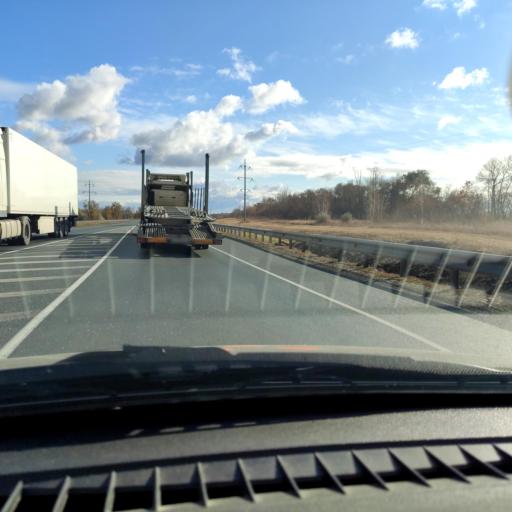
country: RU
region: Samara
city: Varlamovo
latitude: 53.1946
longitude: 48.3248
